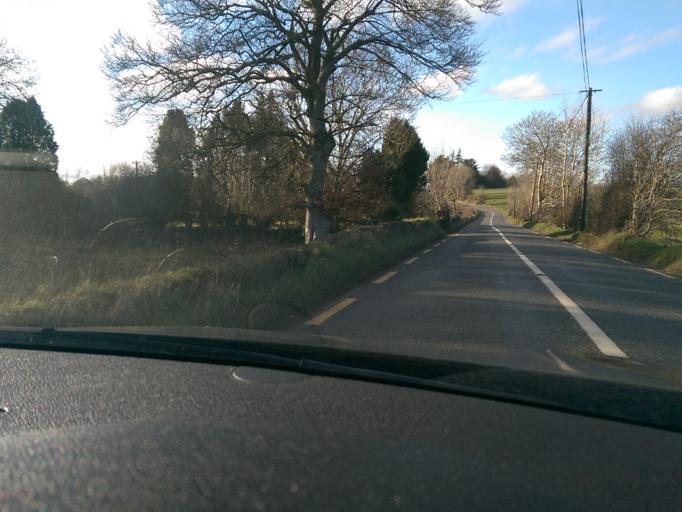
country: IE
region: Connaught
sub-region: Roscommon
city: Roscommon
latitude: 53.7608
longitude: -8.2449
